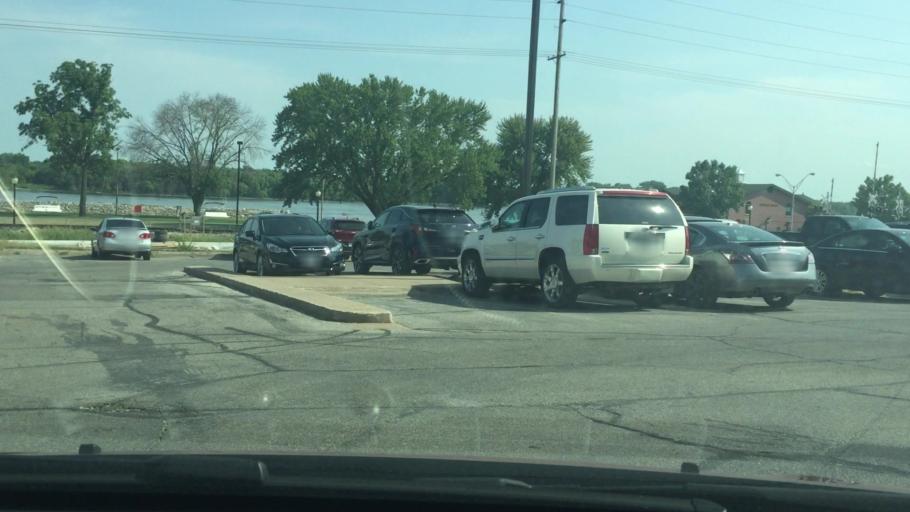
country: US
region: Iowa
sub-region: Muscatine County
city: Muscatine
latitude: 41.4225
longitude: -91.0423
